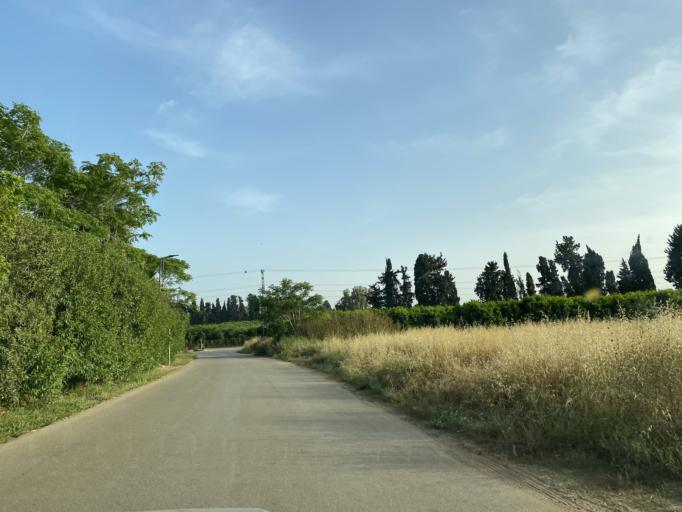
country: IL
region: Tel Aviv
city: Herzliyya
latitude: 32.1557
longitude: 34.8287
